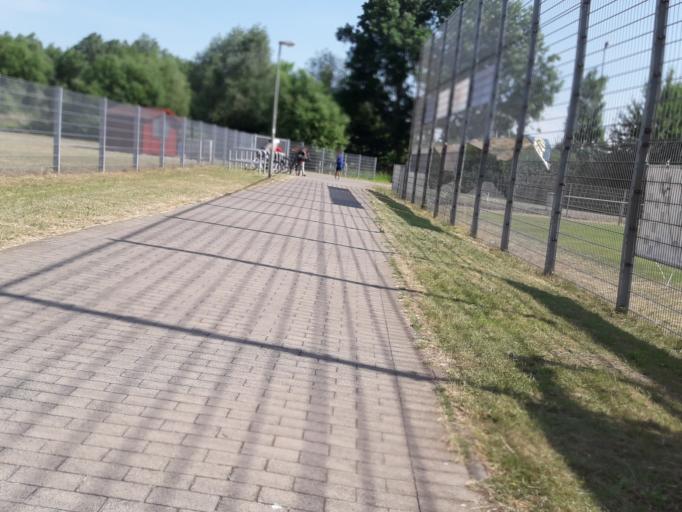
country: DE
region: North Rhine-Westphalia
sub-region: Regierungsbezirk Detmold
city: Paderborn
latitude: 51.7344
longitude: 8.7595
